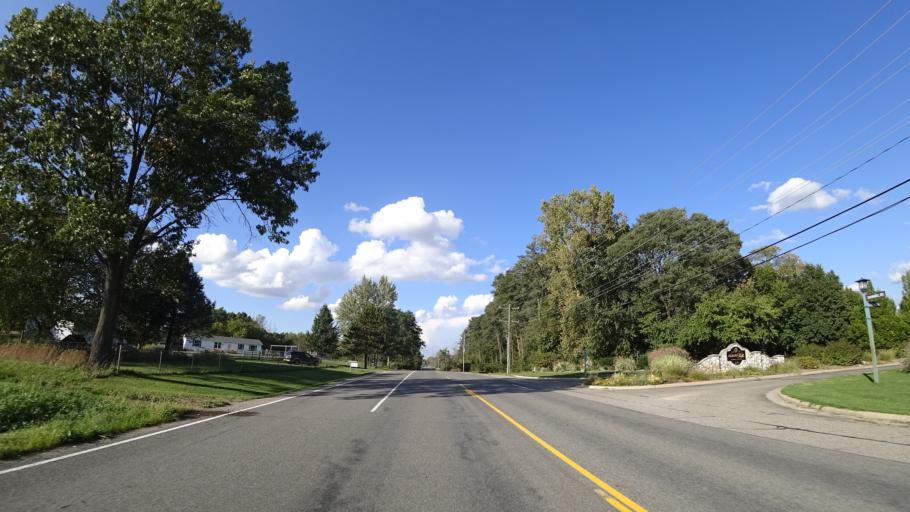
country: US
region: Michigan
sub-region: Saint Joseph County
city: Centreville
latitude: 41.9007
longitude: -85.5070
